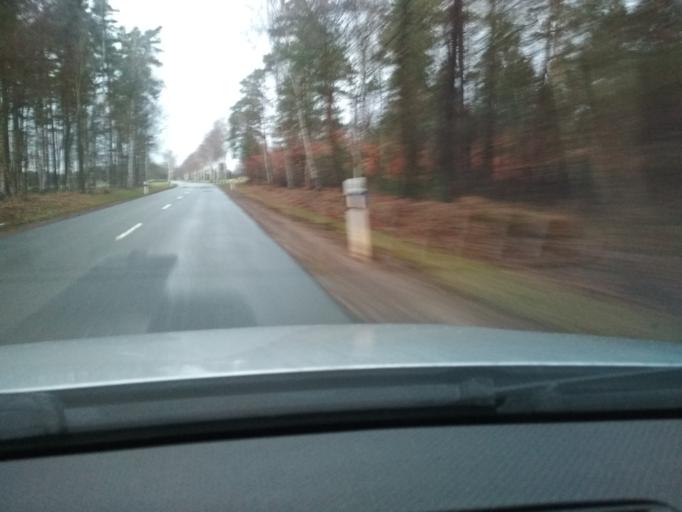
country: DE
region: Lower Saxony
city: Bokensdorf
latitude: 52.5344
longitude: 10.7247
